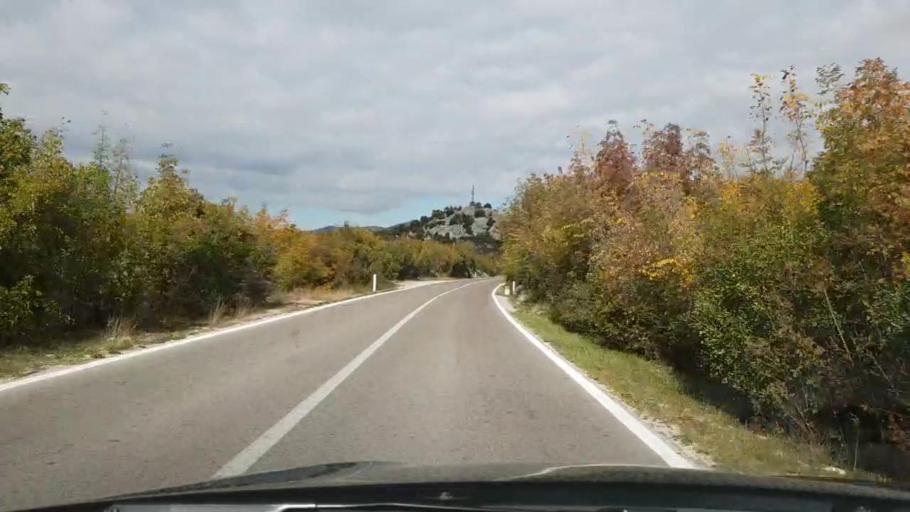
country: HR
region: Dubrovacko-Neretvanska
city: Cibaca
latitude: 42.6812
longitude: 18.2453
